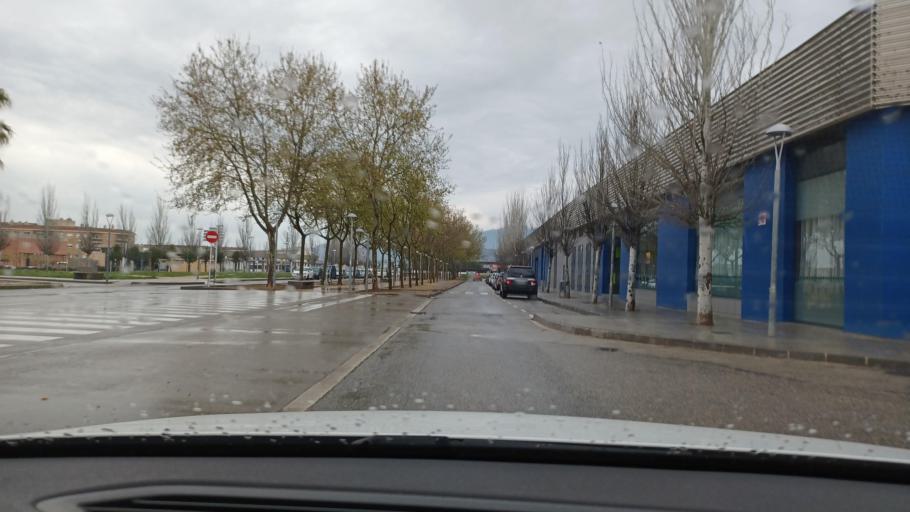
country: ES
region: Catalonia
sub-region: Provincia de Tarragona
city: Amposta
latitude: 40.7082
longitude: 0.5717
